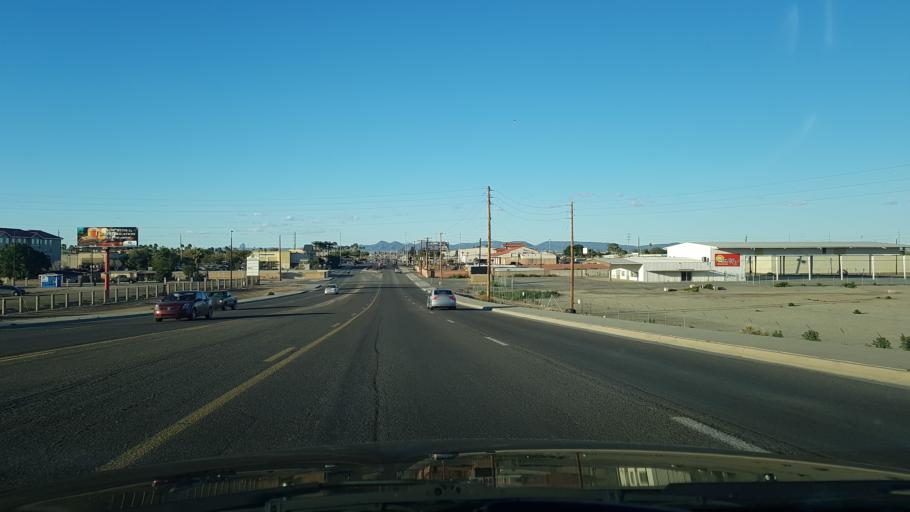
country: US
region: Arizona
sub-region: Yuma County
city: Yuma
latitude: 32.6949
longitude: -114.5988
